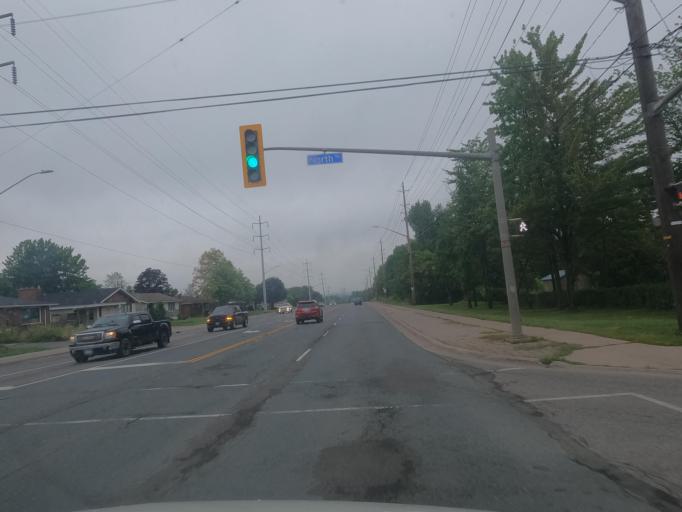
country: CA
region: Ontario
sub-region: Algoma
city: Sault Ste. Marie
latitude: 46.5385
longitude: -84.3353
